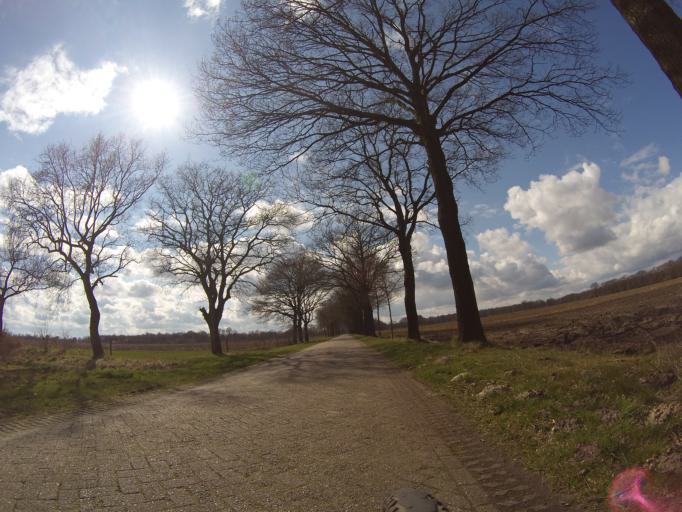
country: NL
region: Drenthe
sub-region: Gemeente Coevorden
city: Dalen
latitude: 52.7472
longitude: 6.6668
